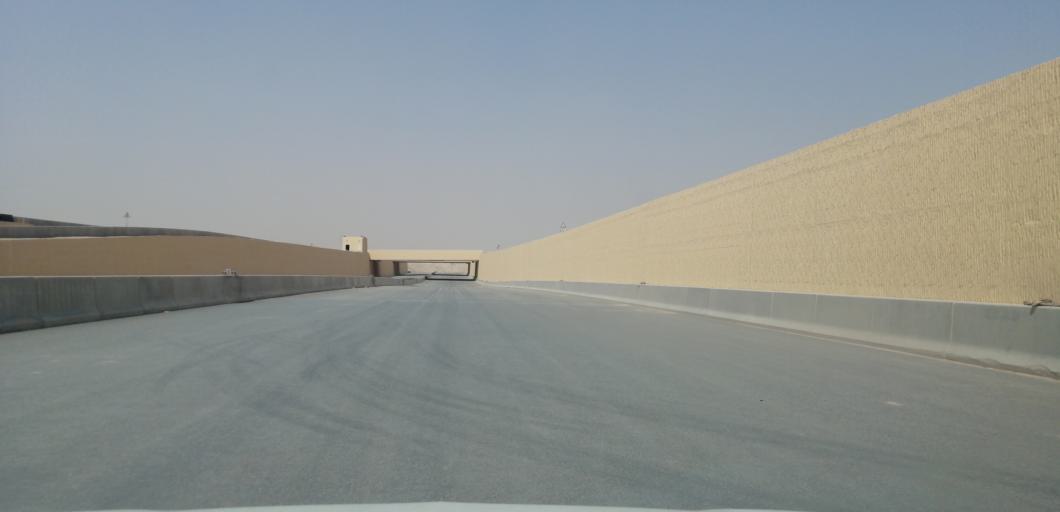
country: KW
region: Muhafazat al Jahra'
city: Al Jahra'
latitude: 29.4538
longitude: 47.5526
